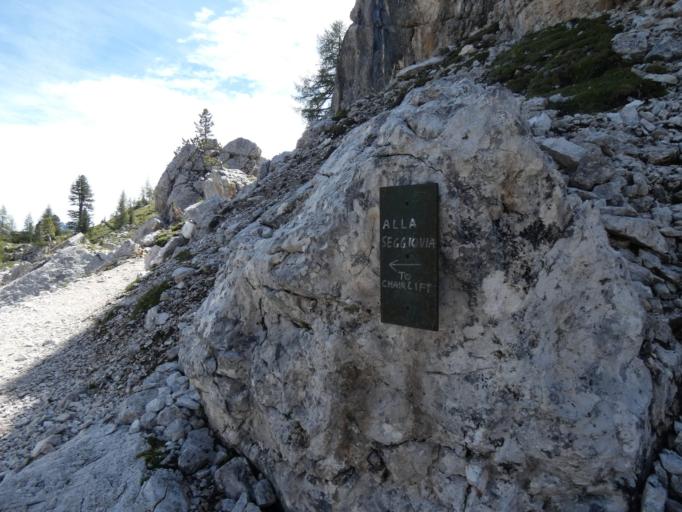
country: IT
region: Veneto
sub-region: Provincia di Belluno
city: Selva di Cadore
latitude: 46.5109
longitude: 12.0517
